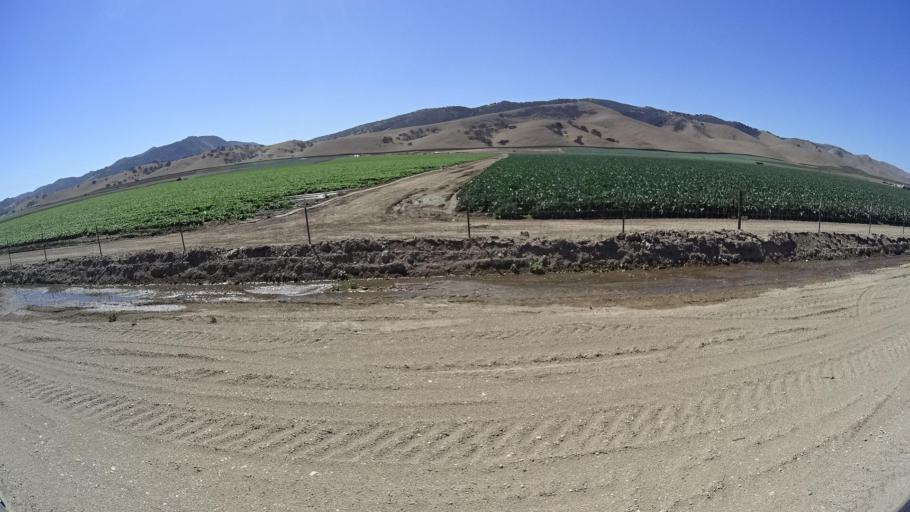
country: US
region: California
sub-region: Monterey County
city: King City
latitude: 36.2467
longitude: -121.1907
